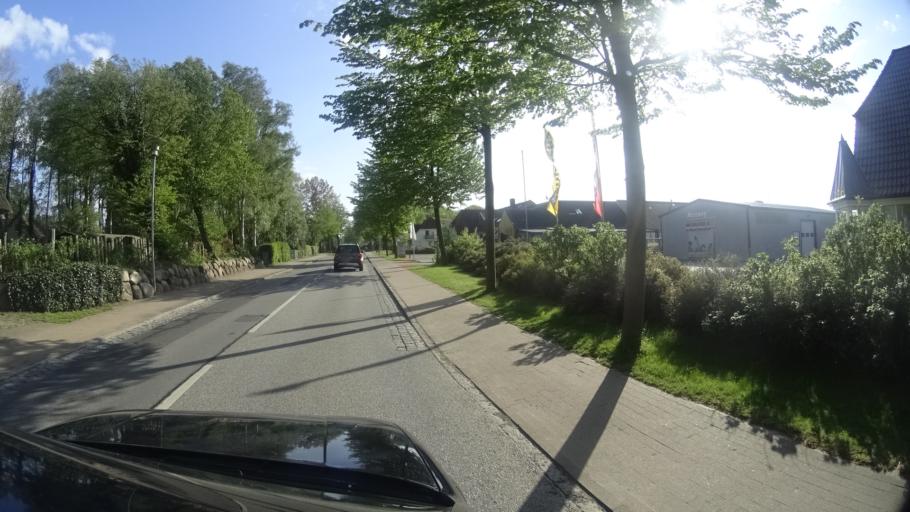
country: DE
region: Mecklenburg-Vorpommern
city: Ostseebad Dierhagen
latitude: 54.3510
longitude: 12.4028
